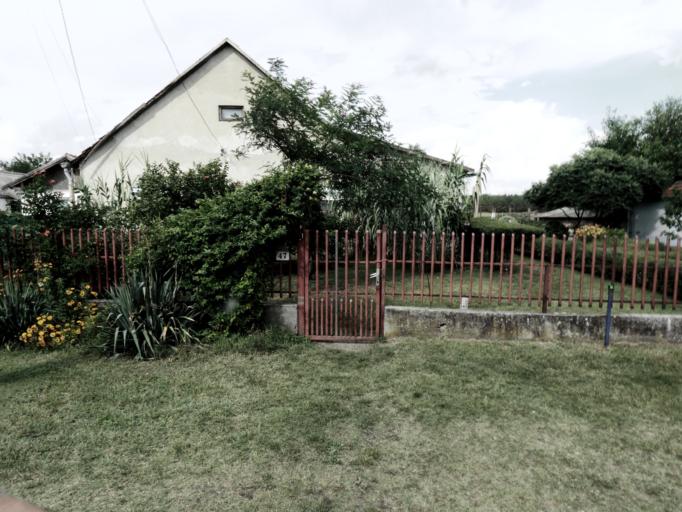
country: HU
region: Pest
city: Taborfalva
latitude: 47.1197
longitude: 19.4751
